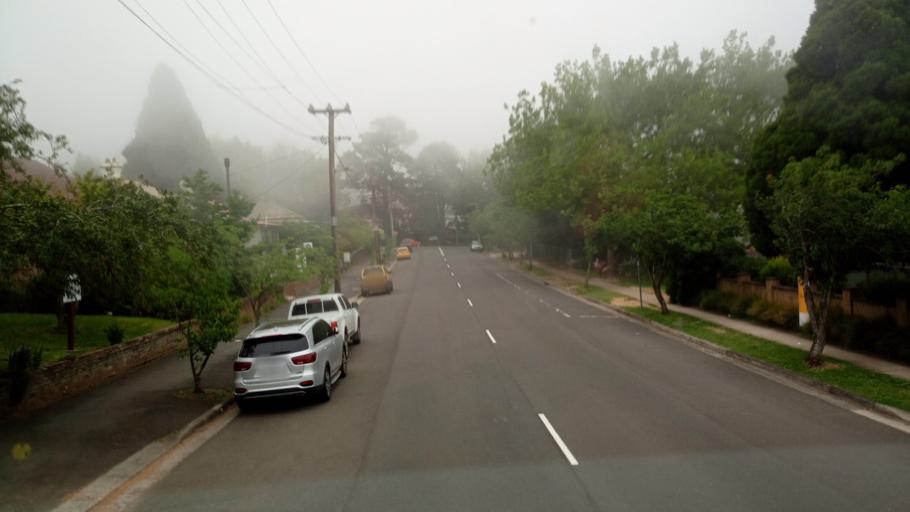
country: AU
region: New South Wales
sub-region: Blue Mountains Municipality
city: Leura
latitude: -33.7133
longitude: 150.3330
